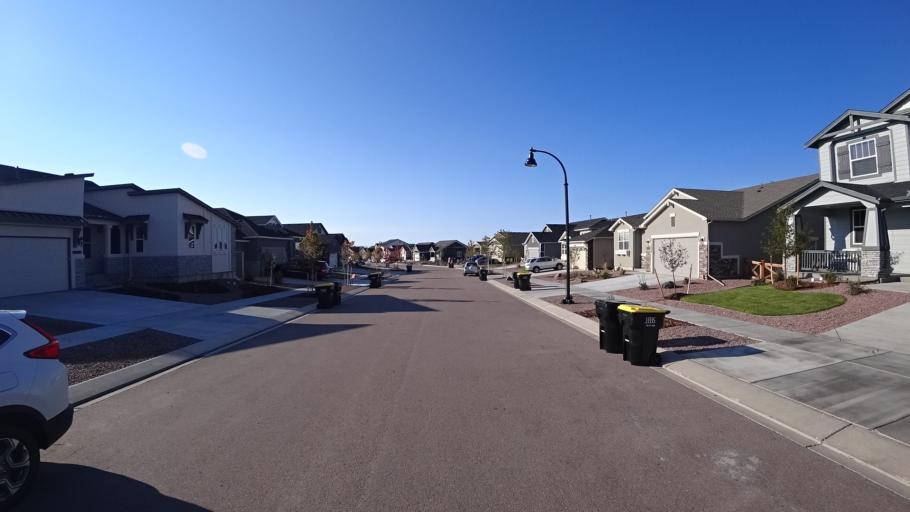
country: US
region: Colorado
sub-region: El Paso County
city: Black Forest
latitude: 38.9364
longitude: -104.6617
